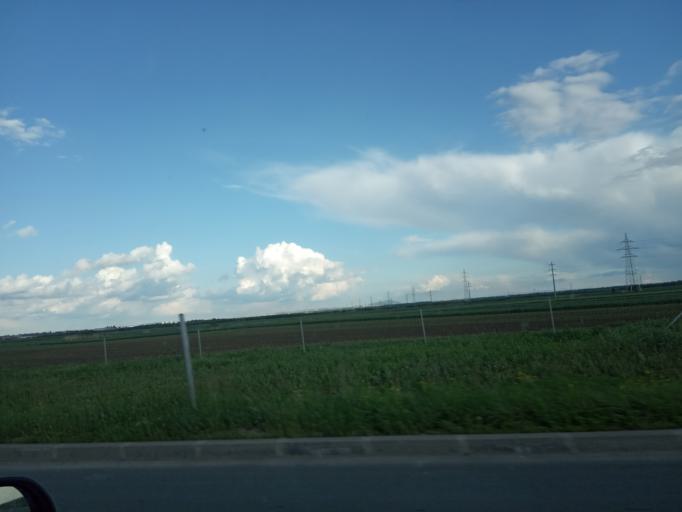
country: RS
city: Dobanovci
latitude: 44.8816
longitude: 20.2741
